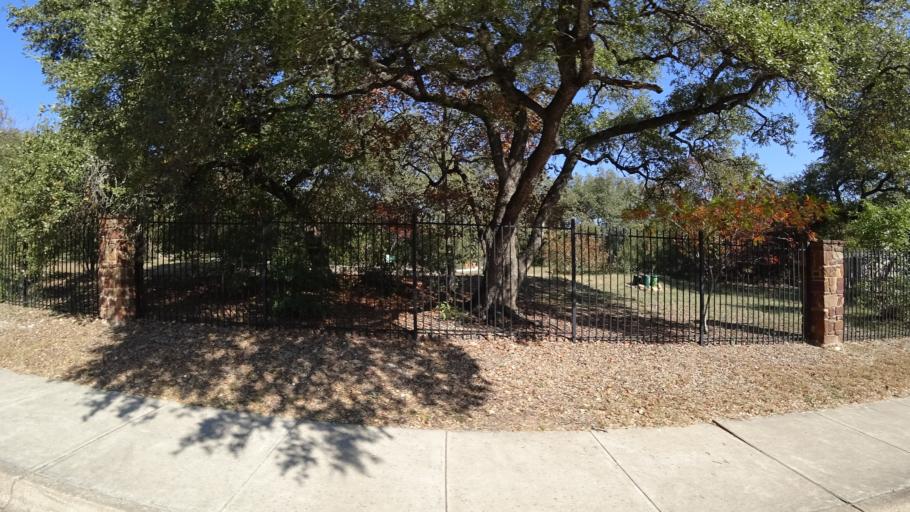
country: US
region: Texas
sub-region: Travis County
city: Barton Creek
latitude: 30.2288
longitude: -97.8724
